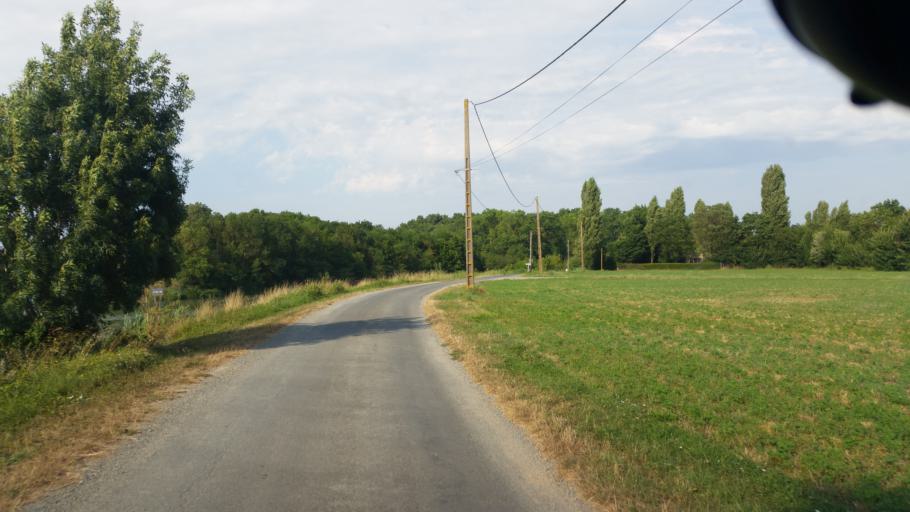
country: FR
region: Pays de la Loire
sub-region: Departement de la Vendee
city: Vix
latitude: 46.3233
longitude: -0.8896
